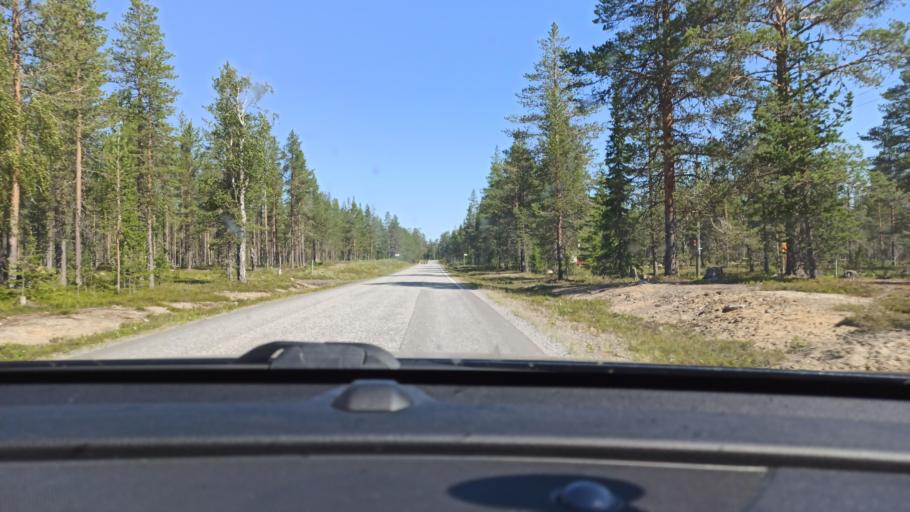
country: FI
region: Lapland
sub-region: Tunturi-Lappi
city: Kolari
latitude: 67.6550
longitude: 24.1638
